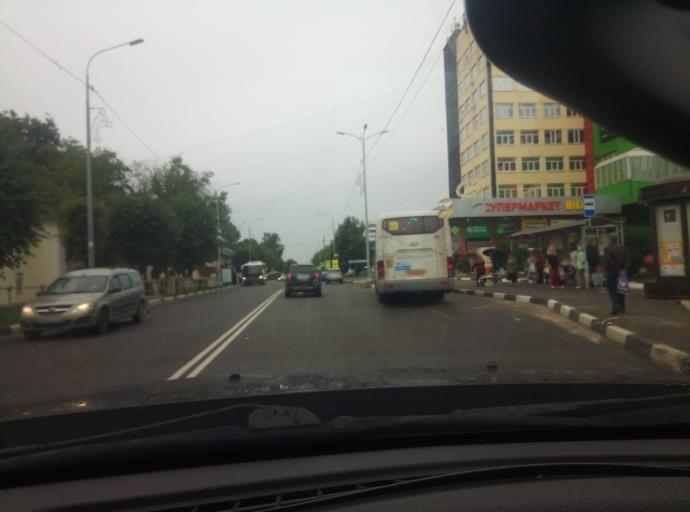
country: RU
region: Moskovskaya
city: Serpukhov
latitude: 54.9153
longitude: 37.4359
